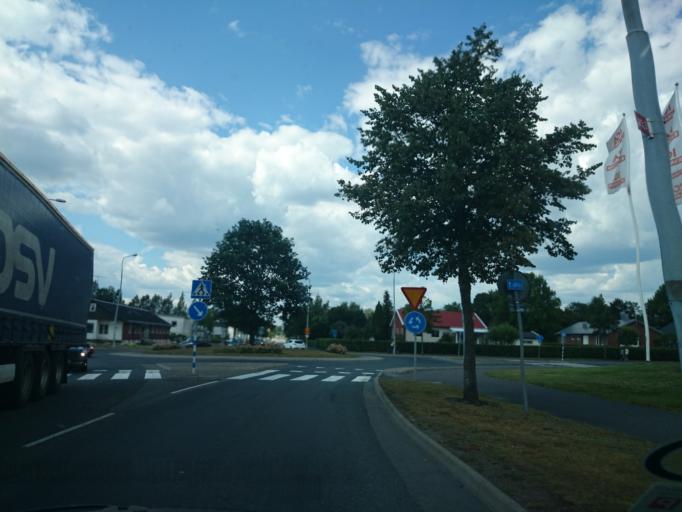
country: SE
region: Joenkoeping
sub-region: Varnamo Kommun
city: Varnamo
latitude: 57.1754
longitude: 14.0607
